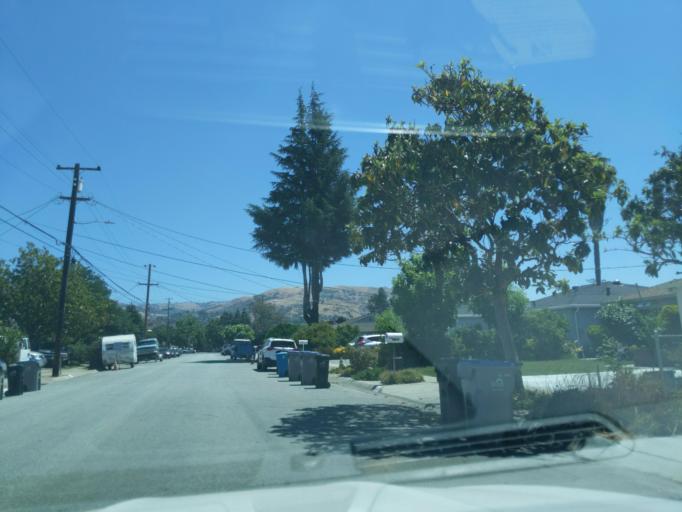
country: US
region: California
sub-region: Santa Clara County
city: Alum Rock
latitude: 37.3757
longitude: -121.8381
